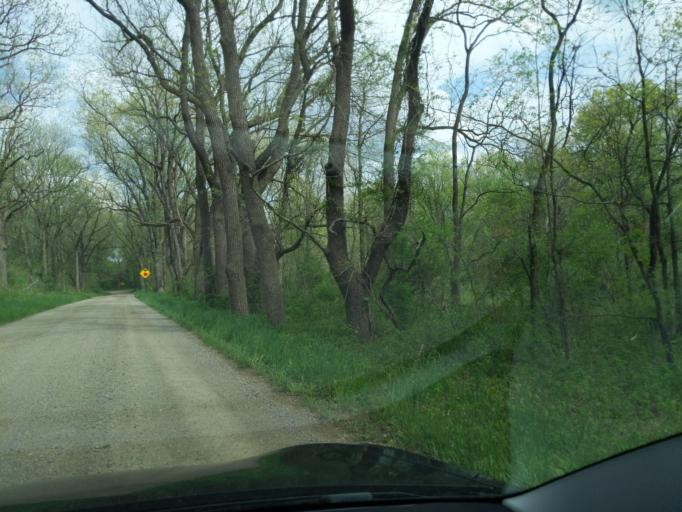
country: US
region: Michigan
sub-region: Washtenaw County
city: Chelsea
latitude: 42.4093
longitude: -84.0628
